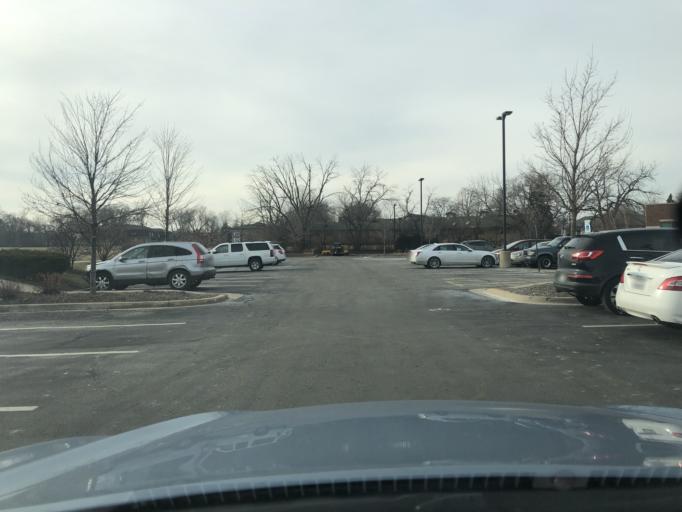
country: US
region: Illinois
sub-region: DuPage County
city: Addison
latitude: 41.9345
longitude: -87.9958
